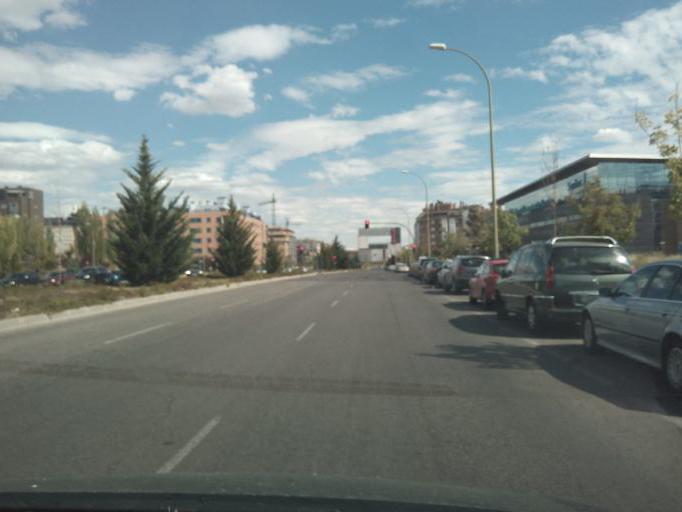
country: ES
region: Madrid
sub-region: Provincia de Madrid
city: Pinar de Chamartin
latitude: 40.4934
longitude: -3.6639
